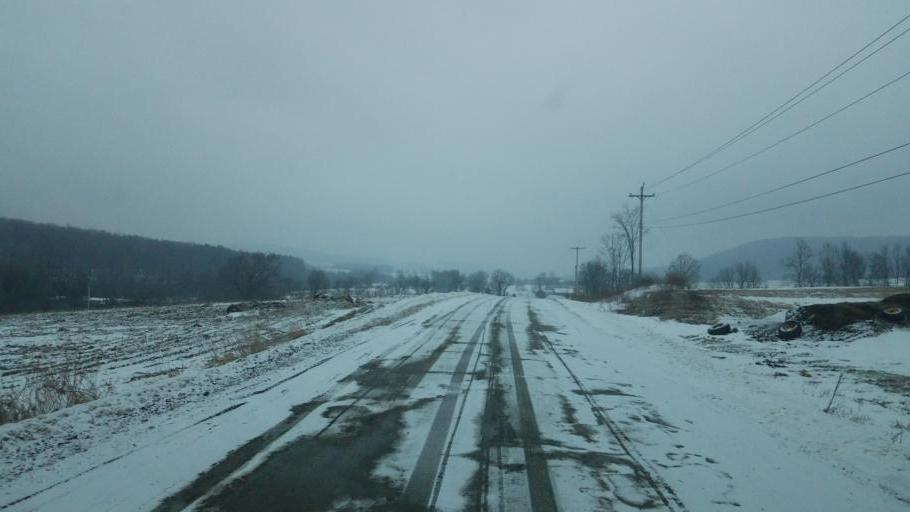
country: US
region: Pennsylvania
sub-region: Tioga County
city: Elkland
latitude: 42.1036
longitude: -77.4661
